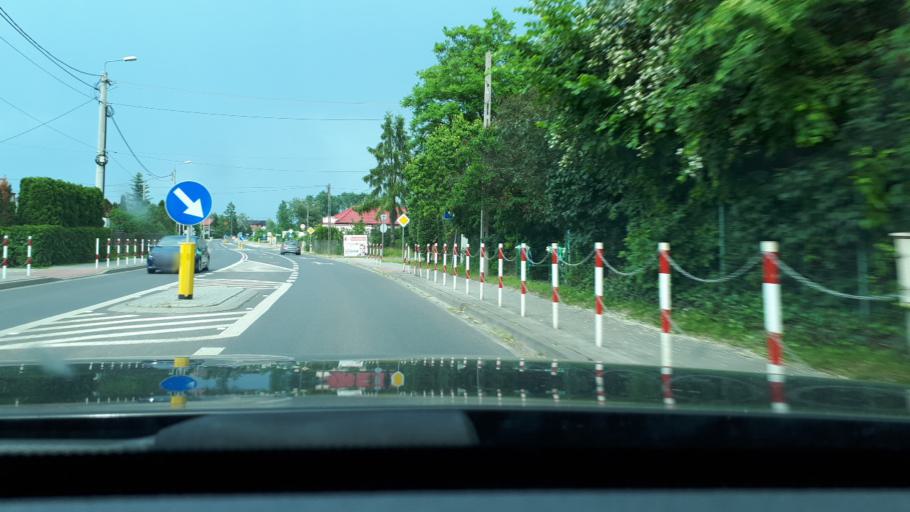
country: PL
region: Masovian Voivodeship
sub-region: Powiat warszawski zachodni
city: Leszno
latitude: 52.2563
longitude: 20.5693
